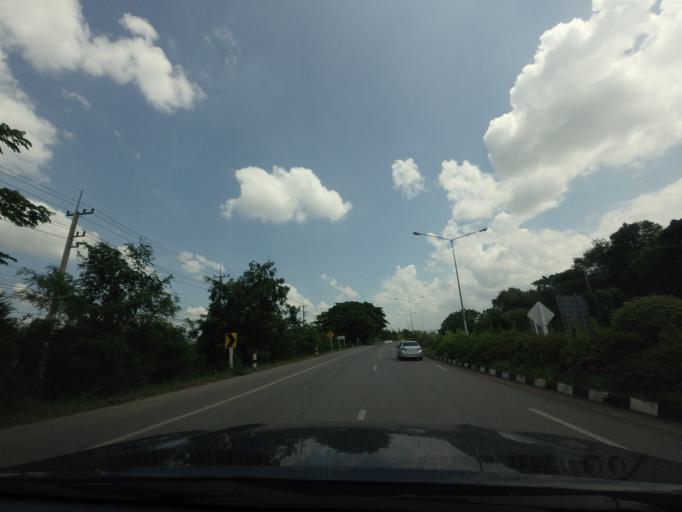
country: TH
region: Phetchabun
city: Phetchabun
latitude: 16.2603
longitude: 101.0532
